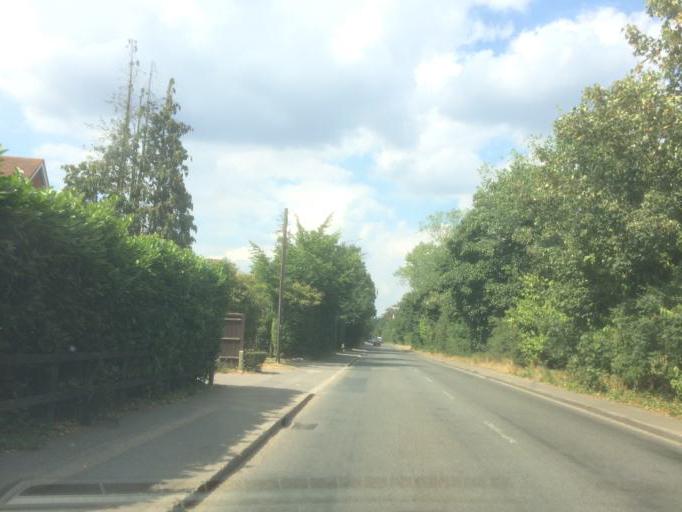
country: GB
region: England
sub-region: Buckinghamshire
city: Farnham Royal
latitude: 51.5403
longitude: -0.6166
